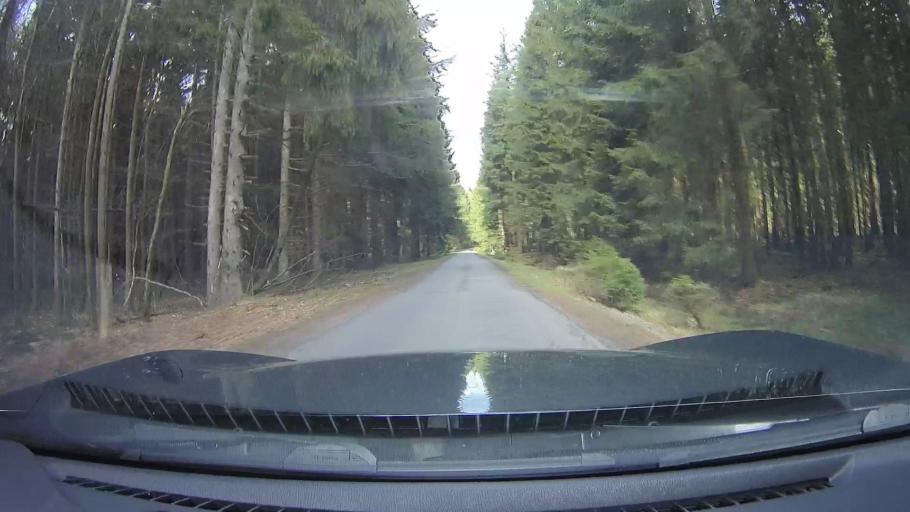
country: DE
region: Hesse
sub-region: Regierungsbezirk Darmstadt
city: Hesseneck
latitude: 49.6086
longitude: 9.0790
